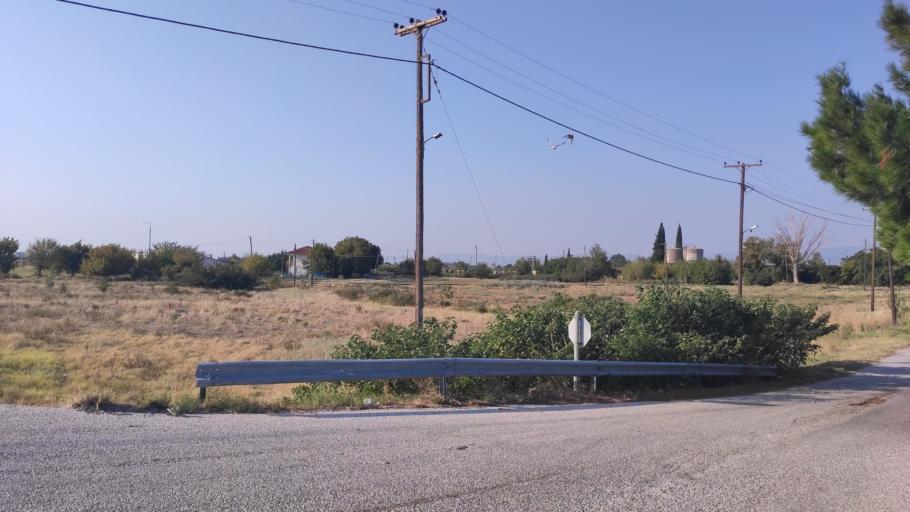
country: GR
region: Central Macedonia
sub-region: Nomos Serron
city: Charopo
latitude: 41.2633
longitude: 23.3474
